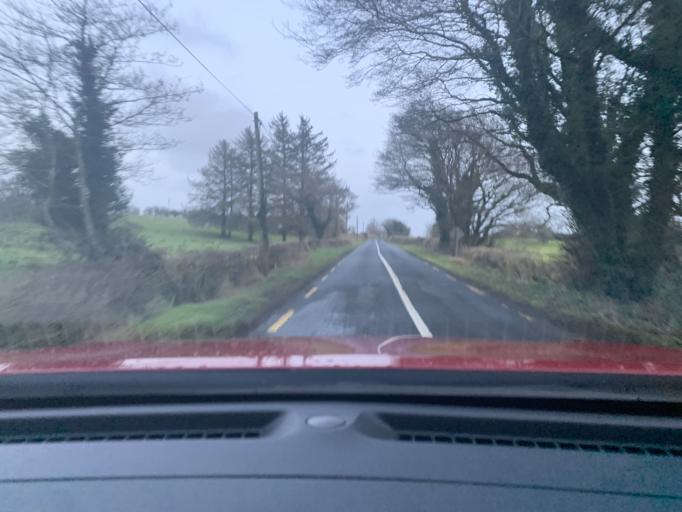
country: IE
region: Connaught
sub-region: Sligo
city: Ballymote
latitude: 54.0353
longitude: -8.4218
